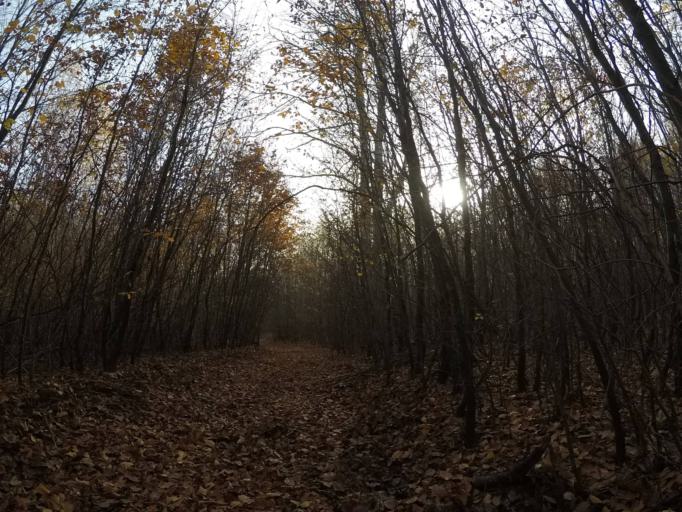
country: SK
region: Presovsky
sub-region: Okres Presov
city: Presov
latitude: 48.9139
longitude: 21.2136
